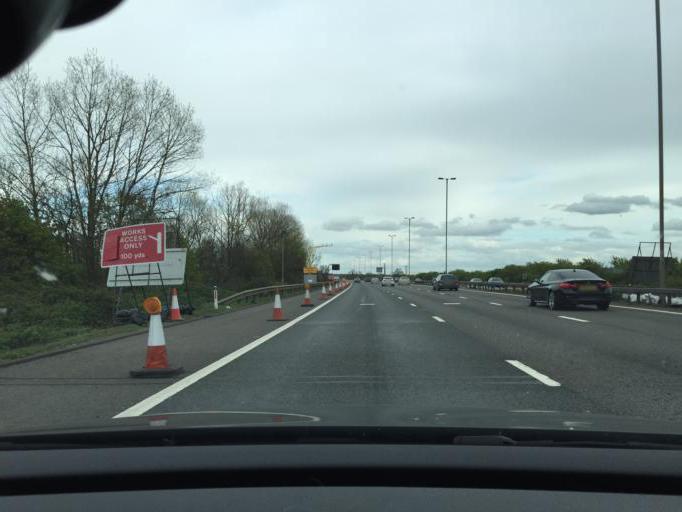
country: GB
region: England
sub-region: West Berkshire
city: Calcot
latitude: 51.4226
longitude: -1.0270
